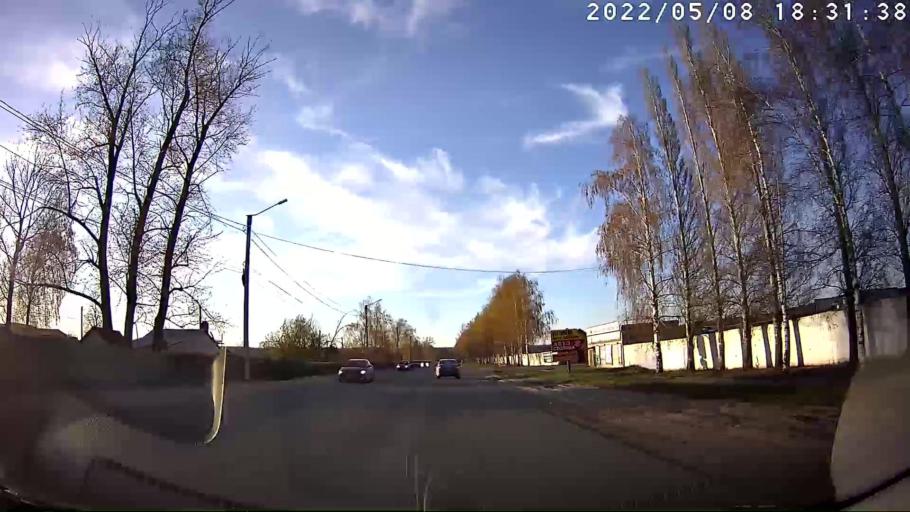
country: RU
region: Mariy-El
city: Volzhsk
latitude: 55.8811
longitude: 48.3598
